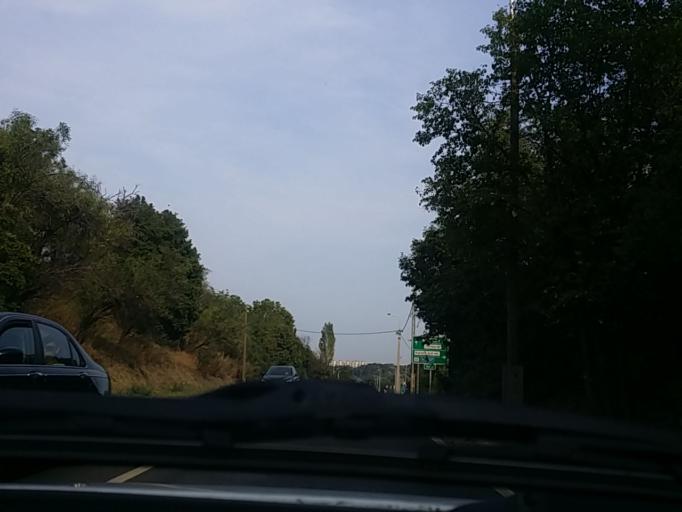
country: HU
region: Pest
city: Budaors
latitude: 47.4631
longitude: 18.9860
